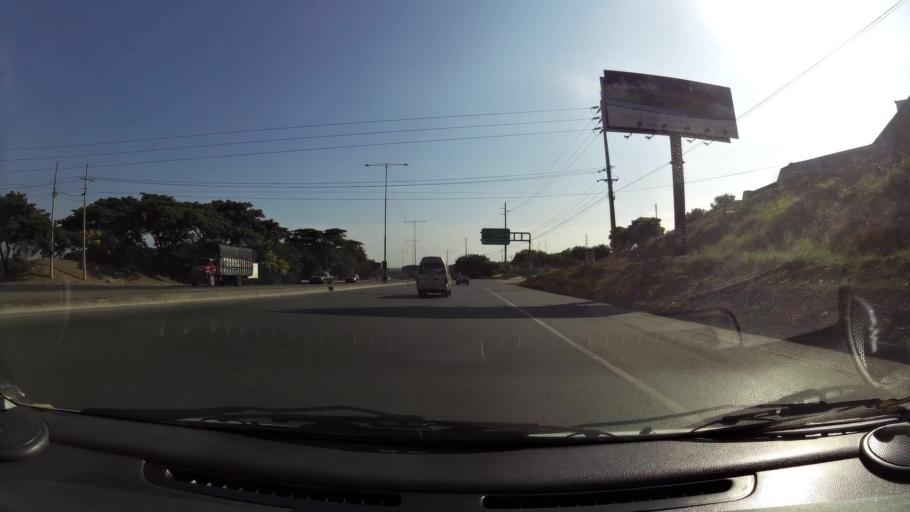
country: EC
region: Guayas
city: Santa Lucia
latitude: -2.1858
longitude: -79.9524
